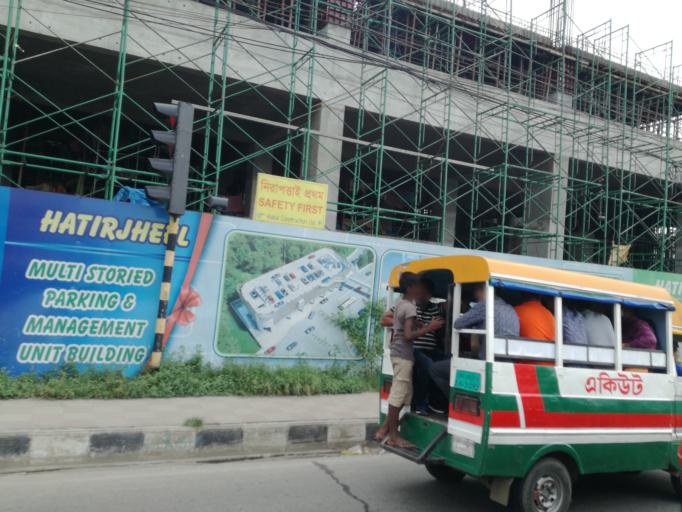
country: BD
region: Dhaka
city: Paltan
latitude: 23.7714
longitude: 90.4131
